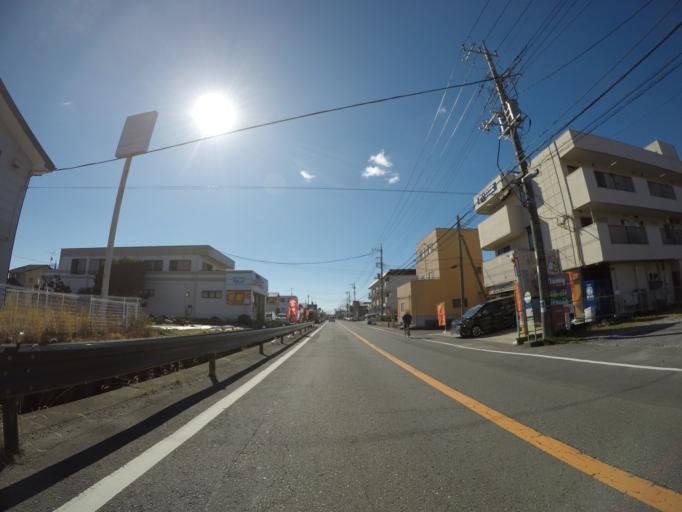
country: JP
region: Shizuoka
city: Numazu
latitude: 35.1375
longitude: 138.8051
